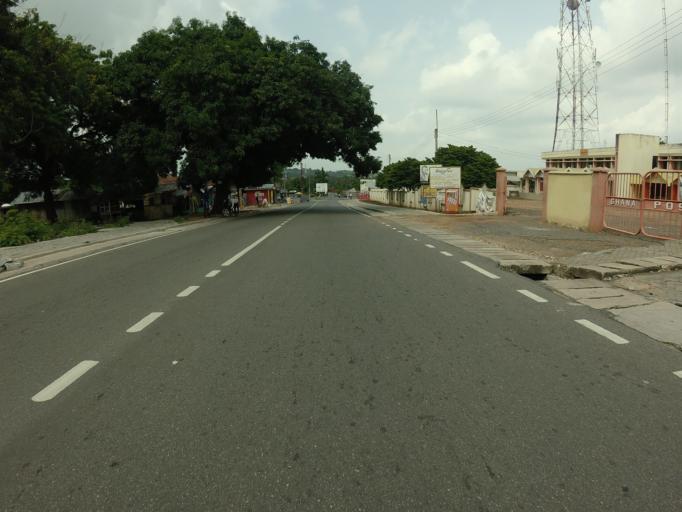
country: GH
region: Volta
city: Ho
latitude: 6.6112
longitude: 0.4695
